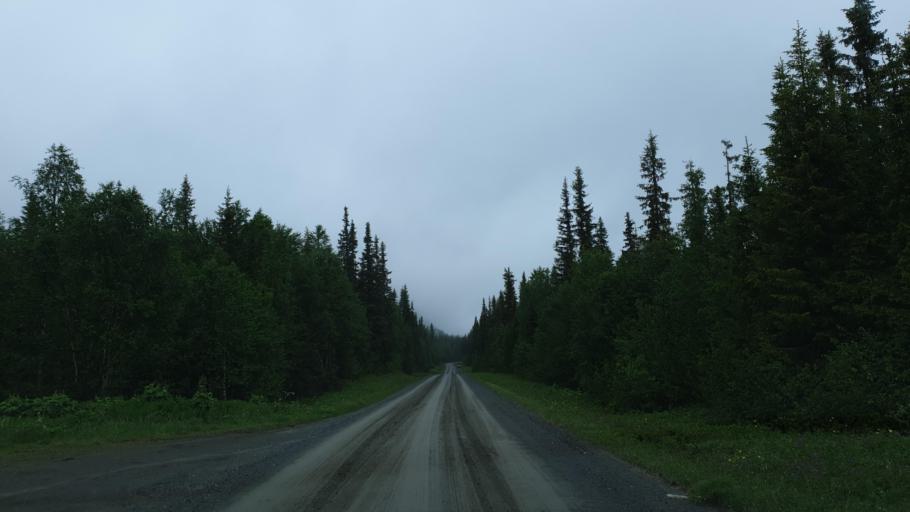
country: SE
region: Vaesterbotten
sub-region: Vilhelmina Kommun
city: Sjoberg
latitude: 65.2777
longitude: 15.8952
